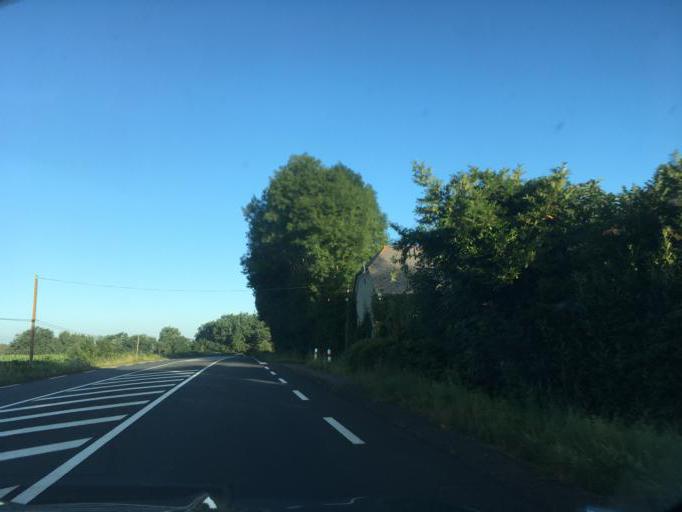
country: FR
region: Aquitaine
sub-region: Departement des Pyrenees-Atlantiques
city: Ger
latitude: 43.2478
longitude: -0.1065
